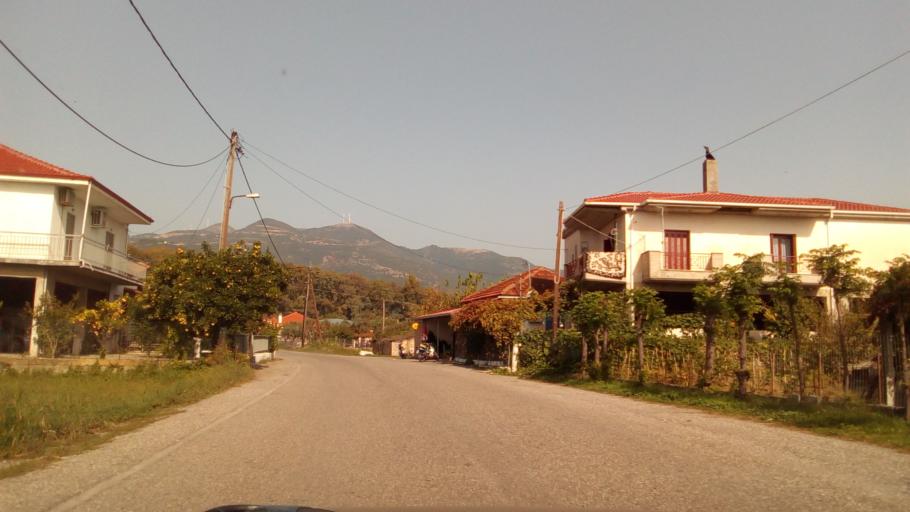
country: GR
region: West Greece
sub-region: Nomos Aitolias kai Akarnanias
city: Nafpaktos
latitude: 38.3960
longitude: 21.8719
